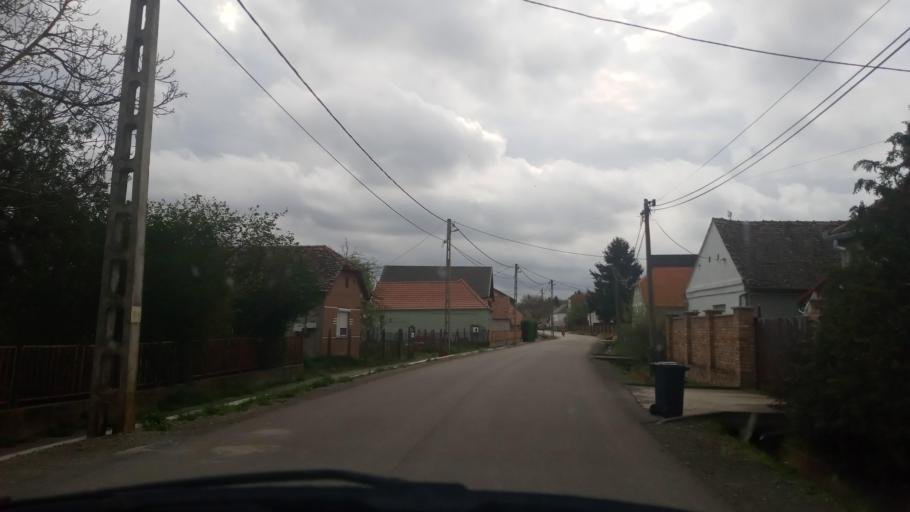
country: HU
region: Baranya
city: Boly
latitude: 45.9755
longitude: 18.4301
